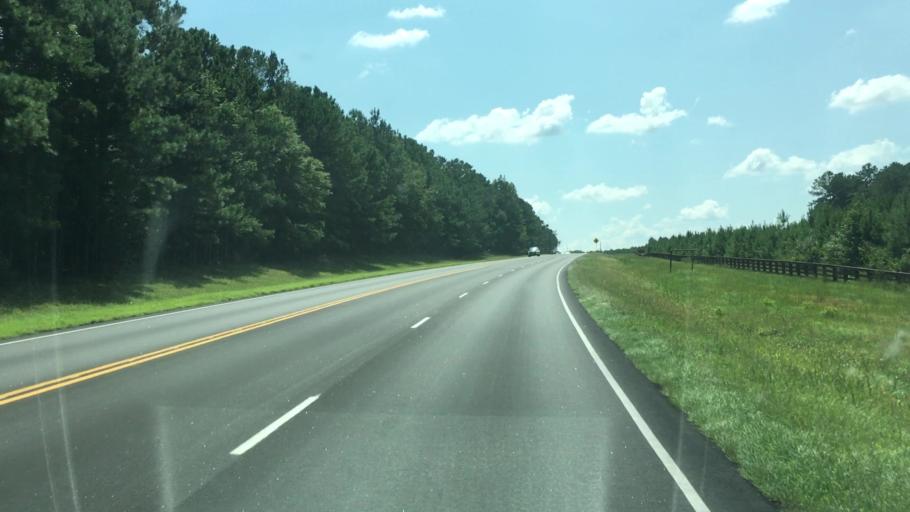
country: US
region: Georgia
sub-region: Morgan County
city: Madison
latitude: 33.7156
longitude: -83.4370
